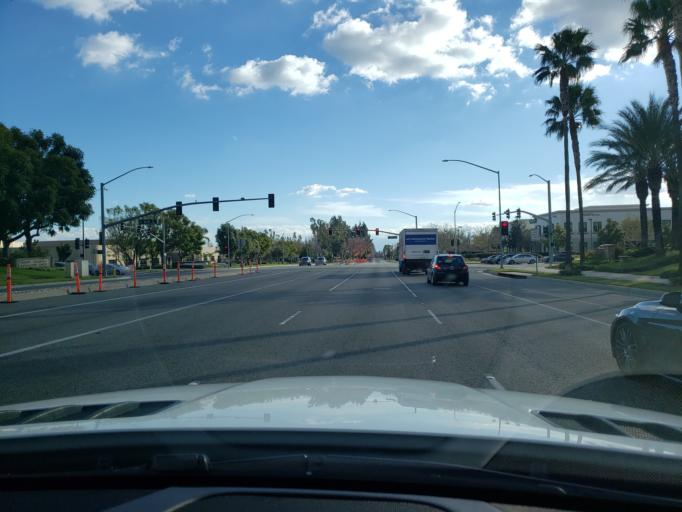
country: US
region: California
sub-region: San Bernardino County
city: Rancho Cucamonga
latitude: 34.0852
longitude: -117.5585
